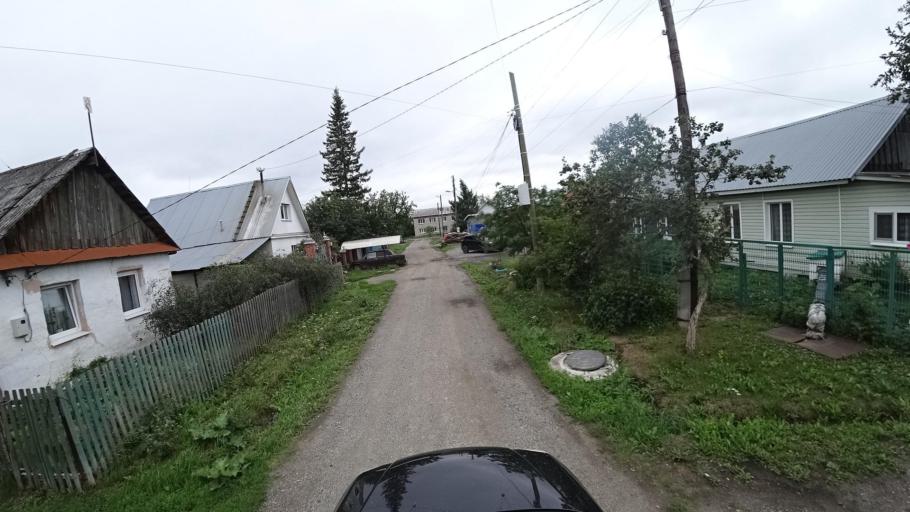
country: RU
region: Sverdlovsk
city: Kamyshlov
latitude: 56.8466
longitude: 62.7670
